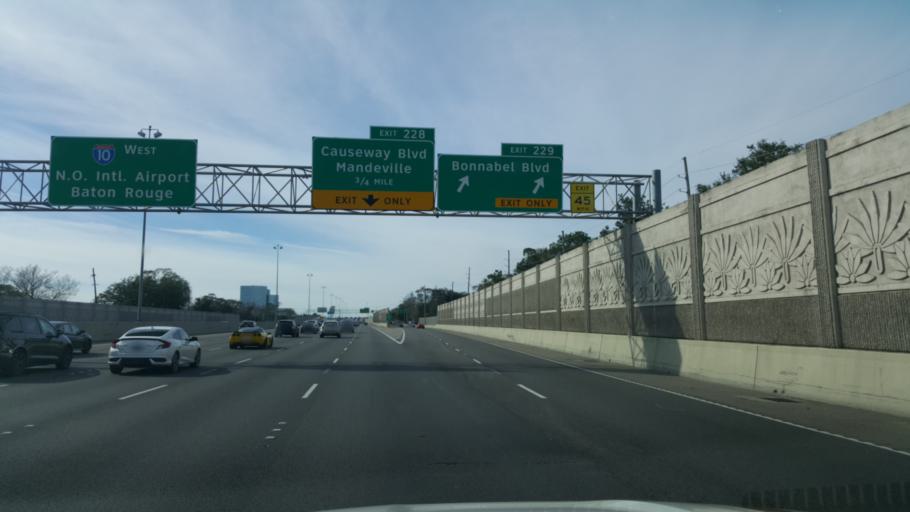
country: US
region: Louisiana
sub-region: Jefferson Parish
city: Metairie
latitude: 29.9970
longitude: -90.1359
